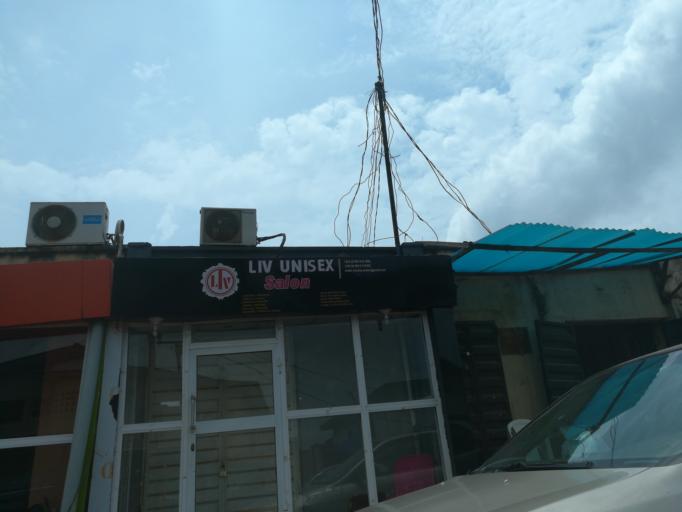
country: NG
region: Lagos
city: Oshodi
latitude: 6.5516
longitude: 3.3230
